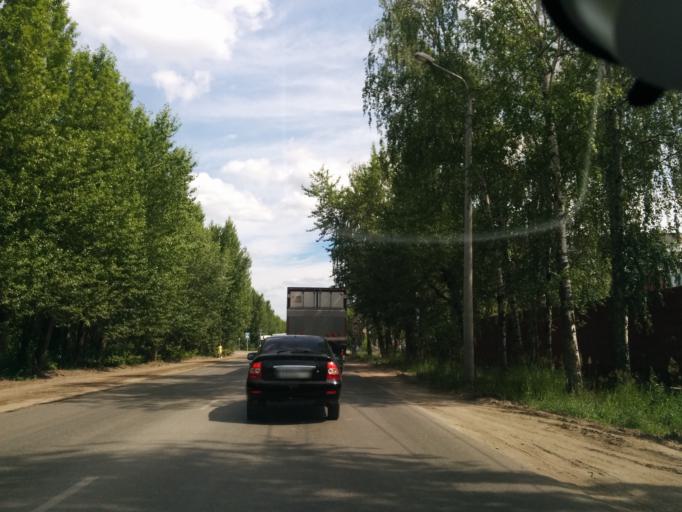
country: RU
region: Perm
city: Overyata
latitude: 58.0131
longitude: 55.9552
